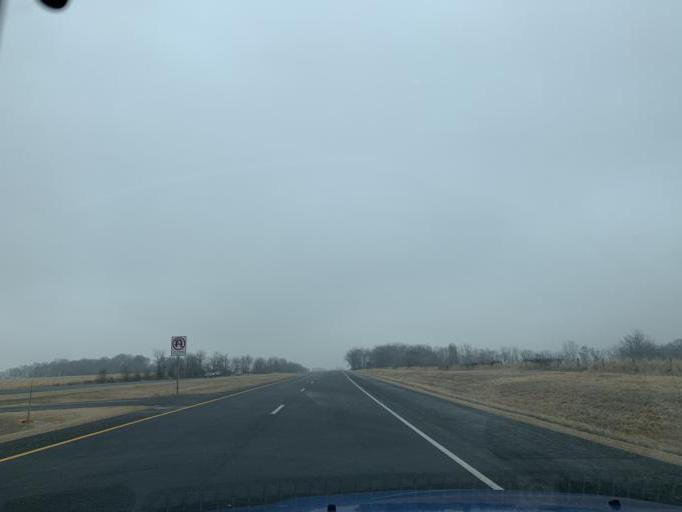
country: US
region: Wisconsin
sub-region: Dane County
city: Sun Prairie
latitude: 43.2457
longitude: -89.1401
